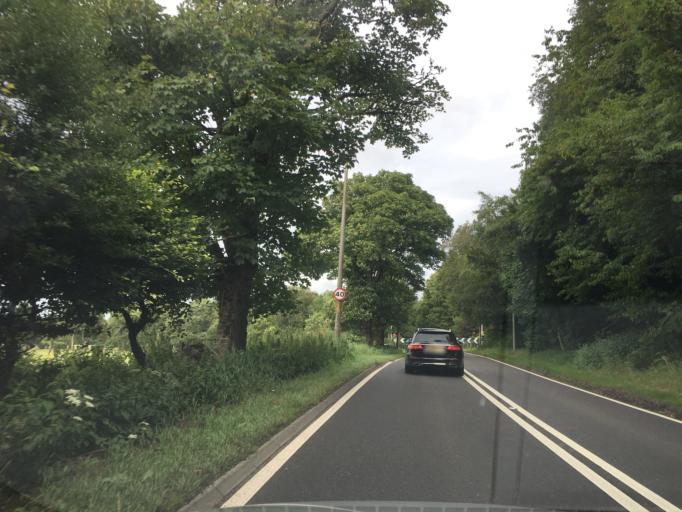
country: GB
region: Scotland
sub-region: South Lanarkshire
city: Biggar
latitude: 55.5590
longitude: -3.6238
